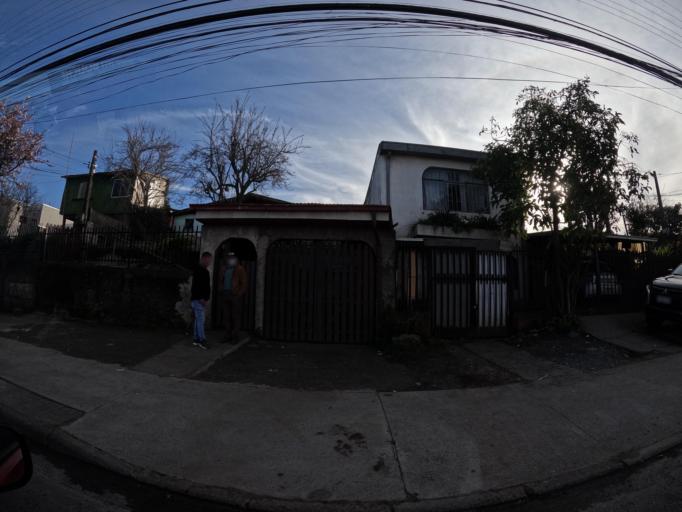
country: CL
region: Biobio
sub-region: Provincia de Concepcion
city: Concepcion
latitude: -36.7913
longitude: -73.0459
